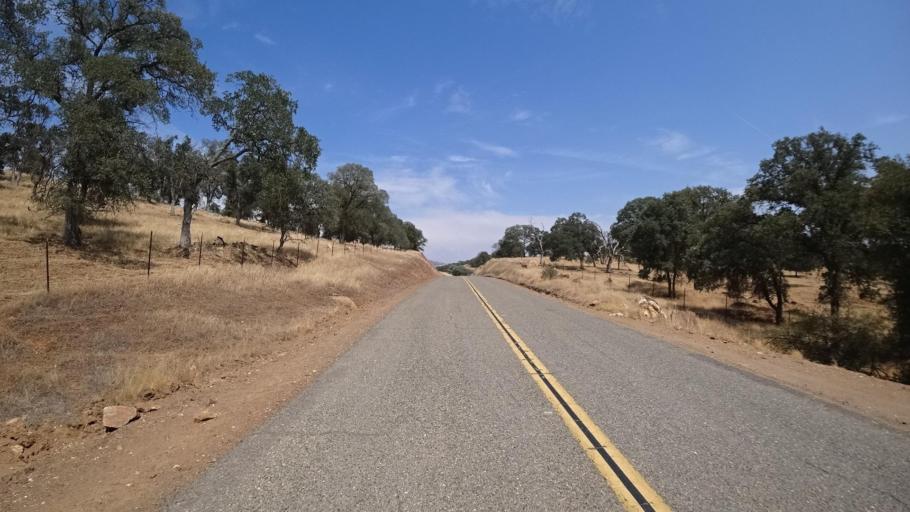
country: US
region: California
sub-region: Merced County
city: Planada
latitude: 37.5201
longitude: -120.2290
